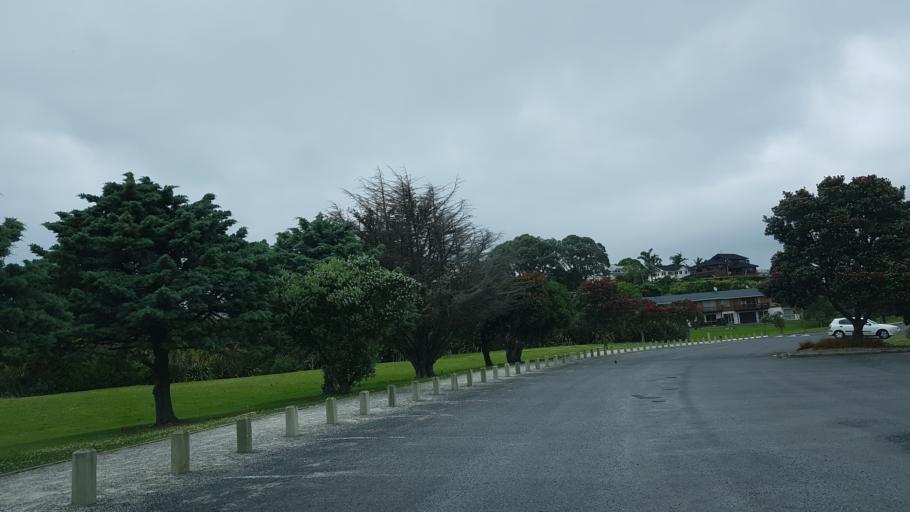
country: NZ
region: Auckland
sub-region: Auckland
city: North Shore
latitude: -36.8092
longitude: 174.7513
